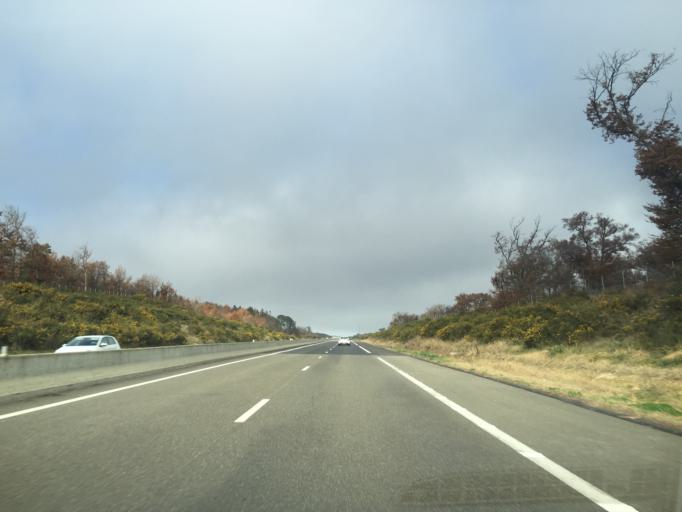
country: FR
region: Aquitaine
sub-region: Departement des Landes
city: Villeneuve-de-Marsan
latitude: 43.8131
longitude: -0.3084
